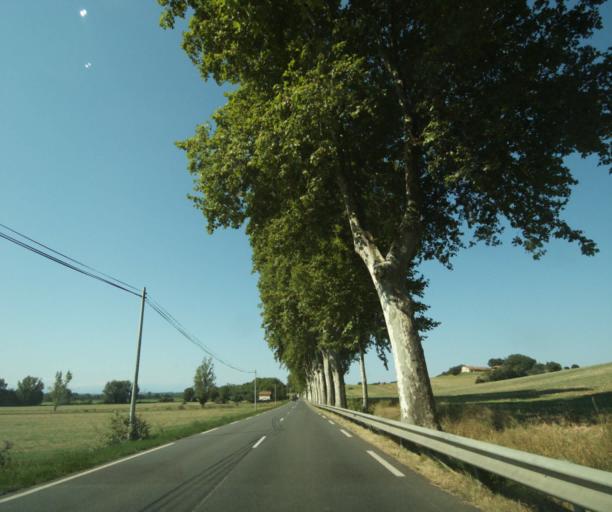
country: FR
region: Midi-Pyrenees
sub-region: Departement de la Haute-Garonne
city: Beaumont-sur-Leze
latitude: 43.3790
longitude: 1.3408
